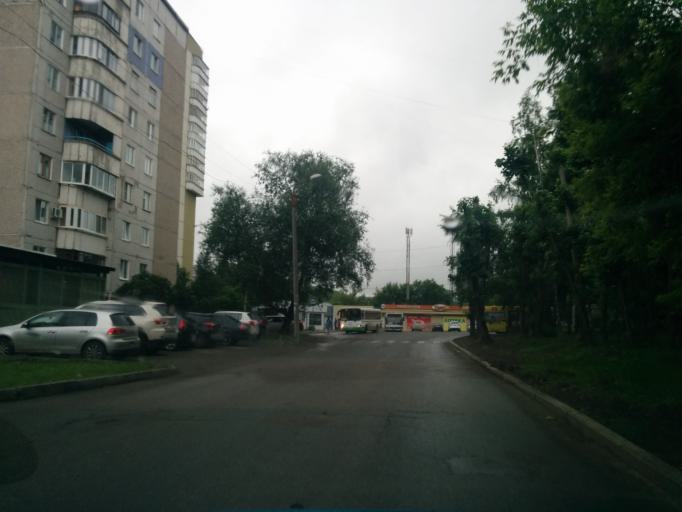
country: RU
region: Perm
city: Perm
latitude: 57.9904
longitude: 56.2331
